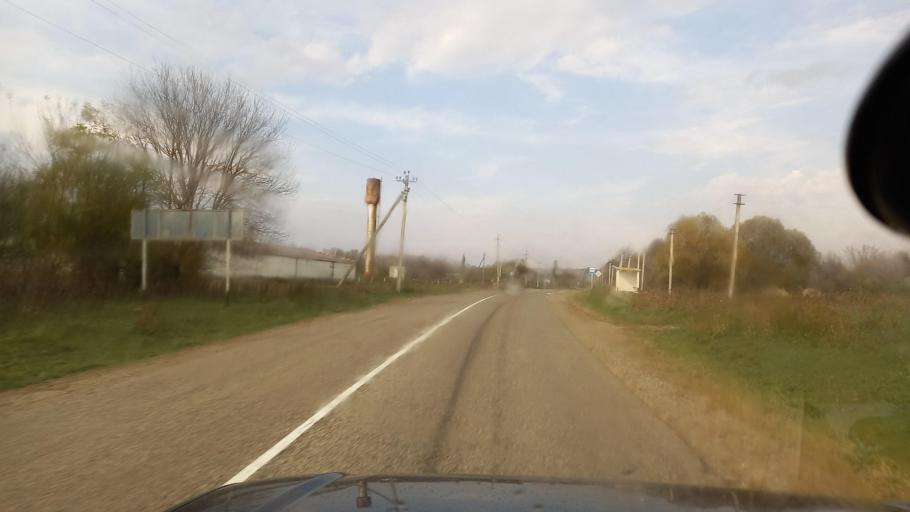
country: RU
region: Krasnodarskiy
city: Gubskaya
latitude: 44.3202
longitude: 40.6067
